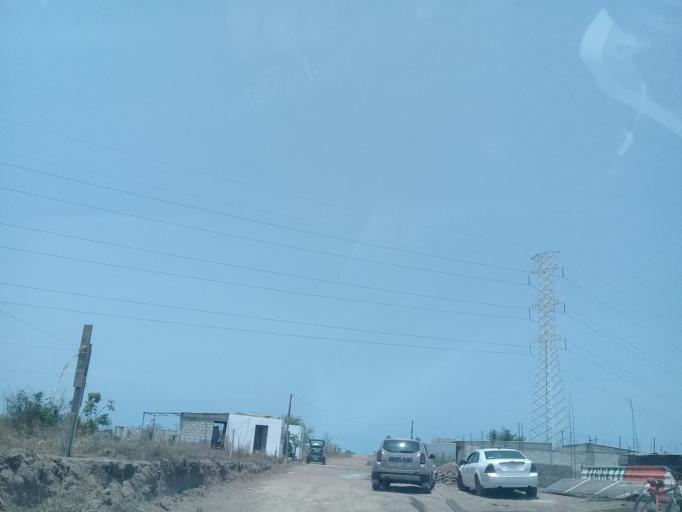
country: MX
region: Veracruz
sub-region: Veracruz
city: Las Amapolas
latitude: 19.1566
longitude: -96.2157
